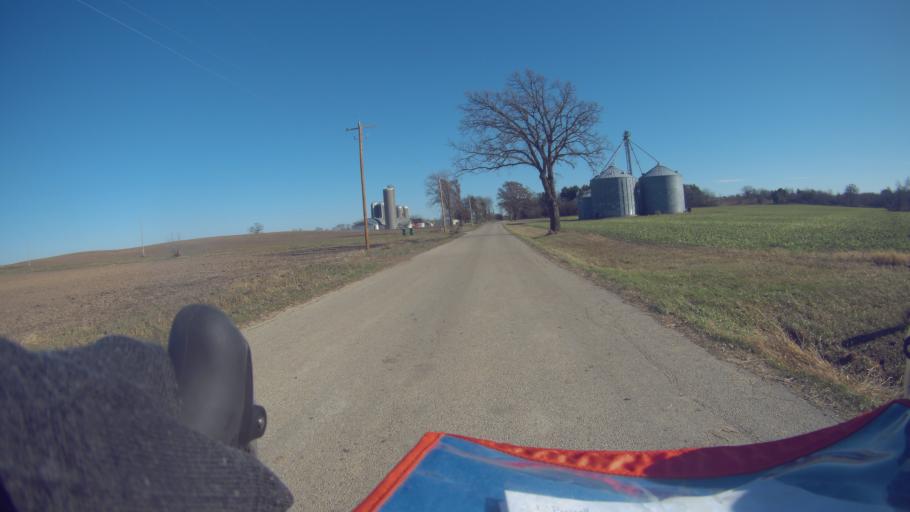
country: US
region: Wisconsin
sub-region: Green County
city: Brooklyn
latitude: 42.8396
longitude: -89.3579
